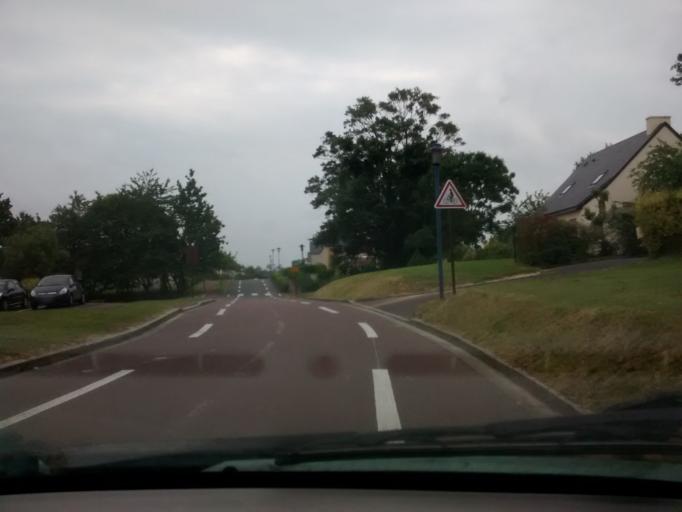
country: FR
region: Lower Normandy
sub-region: Departement de la Manche
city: Saint-Lo
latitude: 49.1057
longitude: -1.0830
